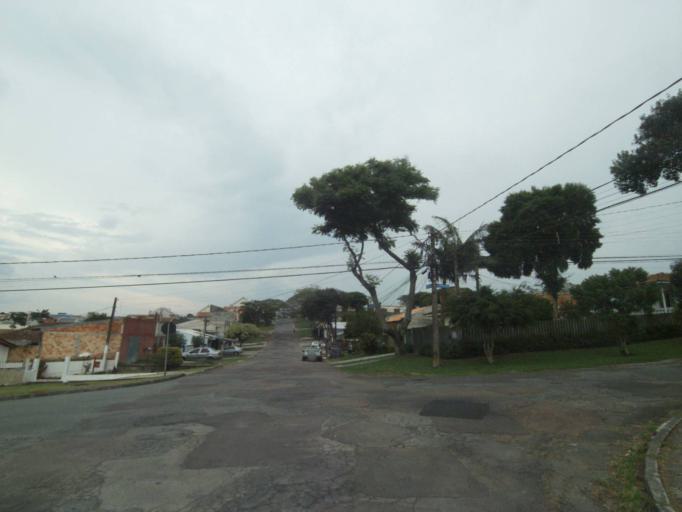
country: BR
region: Parana
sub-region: Pinhais
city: Pinhais
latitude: -25.3950
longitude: -49.2015
